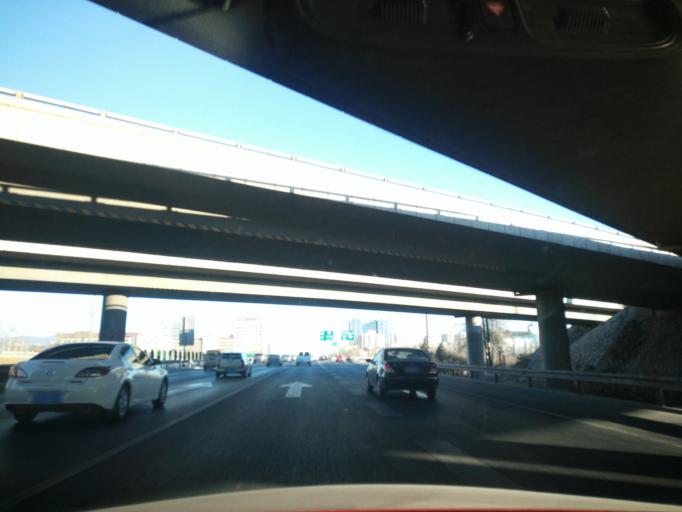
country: CN
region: Beijing
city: Lugu
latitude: 39.8932
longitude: 116.2053
